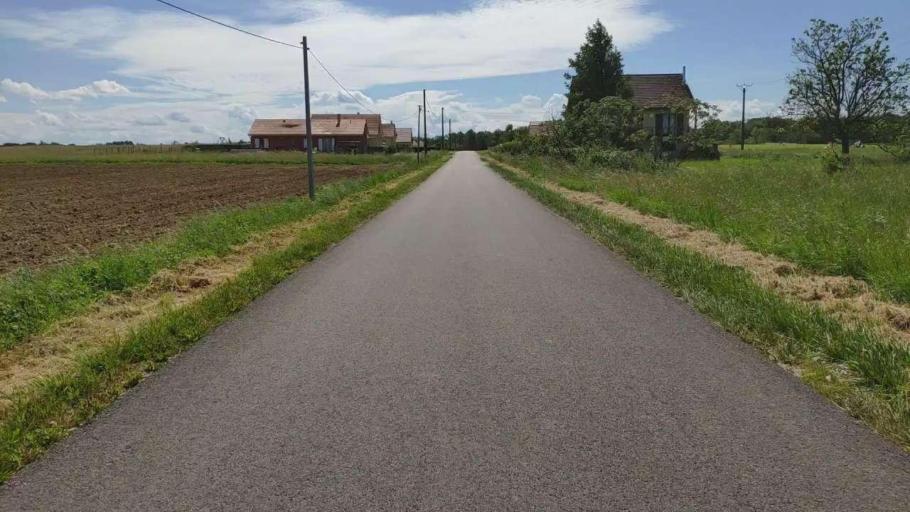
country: FR
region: Franche-Comte
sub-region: Departement du Jura
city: Bletterans
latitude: 46.7082
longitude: 5.4211
